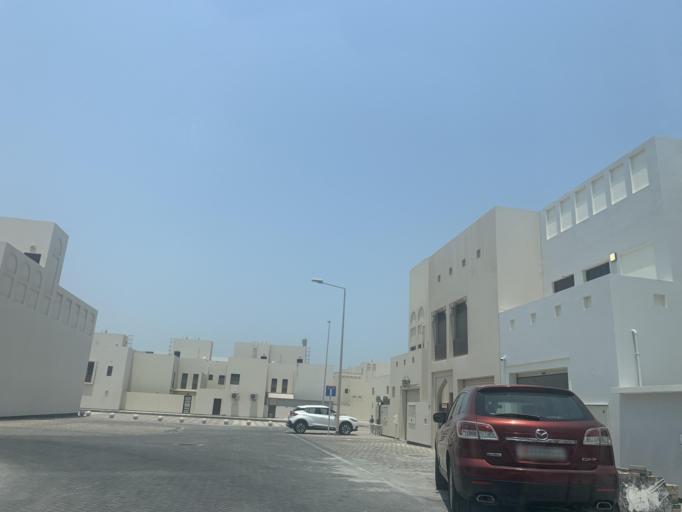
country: BH
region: Muharraq
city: Al Hadd
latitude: 26.2323
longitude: 50.6742
